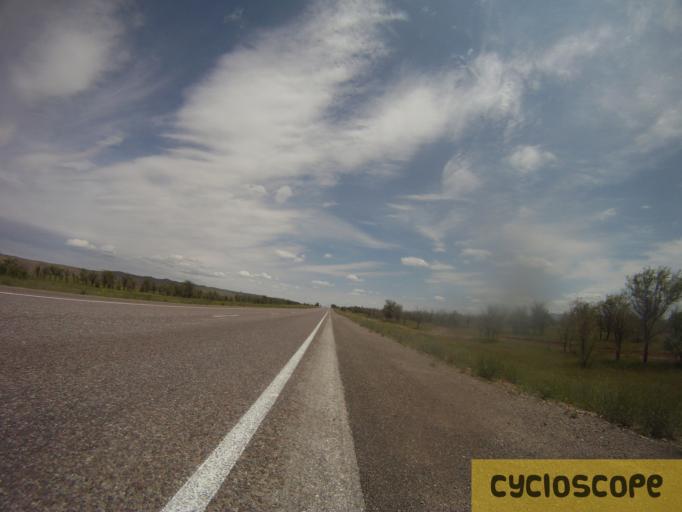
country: KZ
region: Zhambyl
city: Georgiyevka
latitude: 43.3166
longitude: 74.9238
